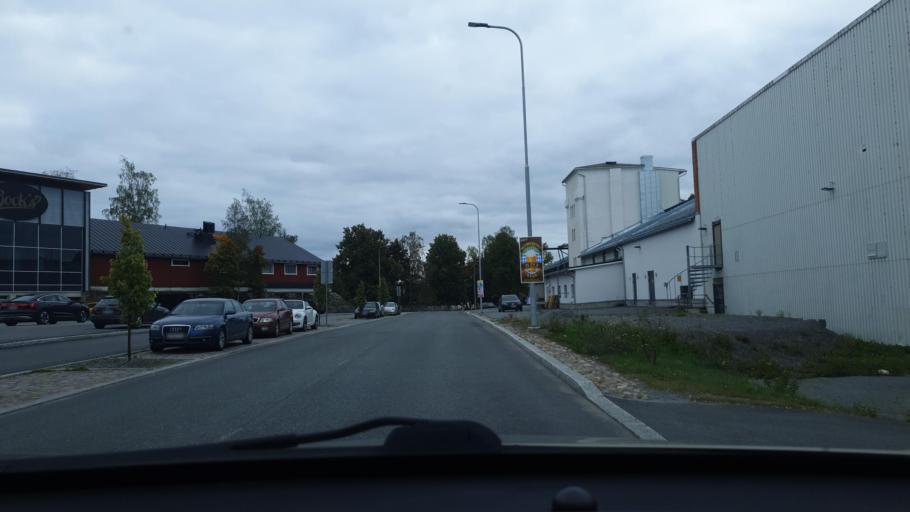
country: FI
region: Ostrobothnia
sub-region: Vaasa
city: Vaasa
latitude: 63.1173
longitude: 21.6198
